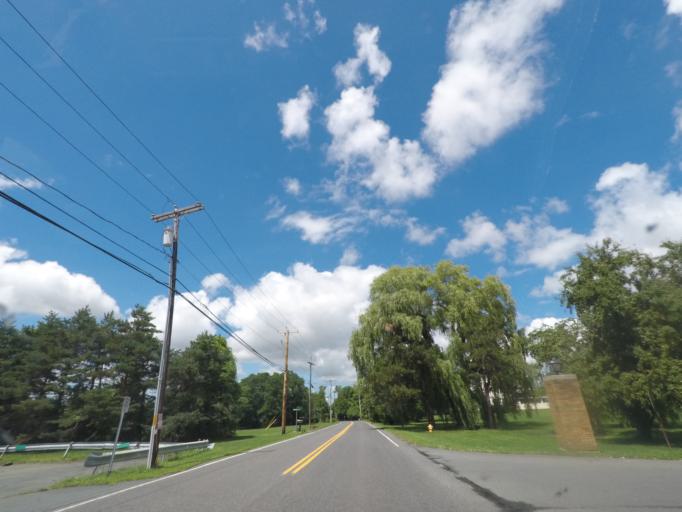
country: US
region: New York
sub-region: Rensselaer County
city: Wynantskill
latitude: 42.6875
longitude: -73.6818
